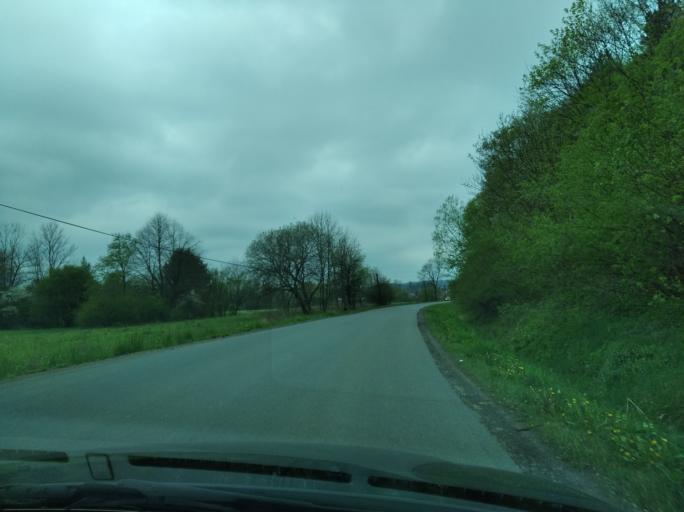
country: PL
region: Subcarpathian Voivodeship
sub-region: Powiat sanocki
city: Sanok
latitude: 49.5976
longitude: 22.1907
